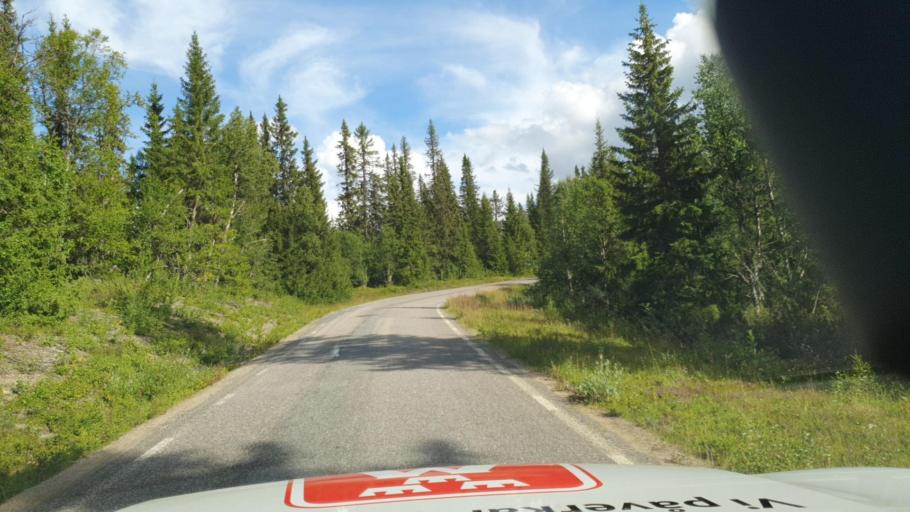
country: NO
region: Hedmark
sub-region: Engerdal
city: Engerdal
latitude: 62.1475
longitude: 12.9956
